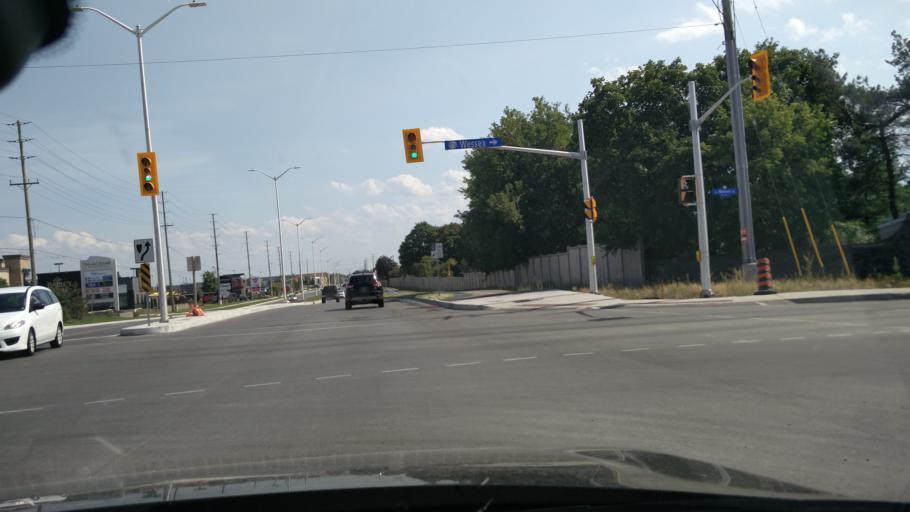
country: CA
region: Ontario
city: Bells Corners
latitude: 45.2750
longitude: -75.7492
